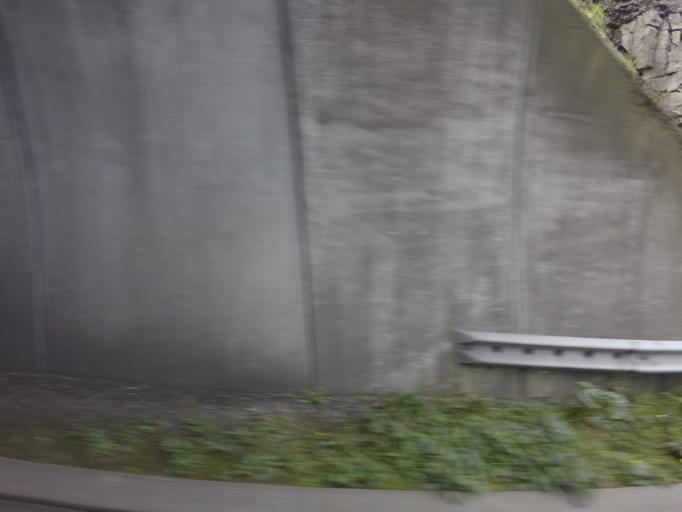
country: FO
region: Eysturoy
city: Eystur
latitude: 62.2074
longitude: -6.6815
